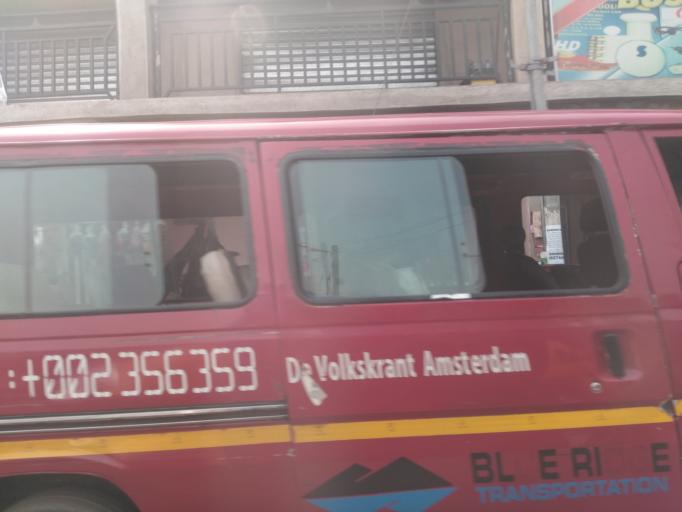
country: GH
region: Ashanti
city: Kumasi
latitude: 6.7043
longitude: -1.6234
